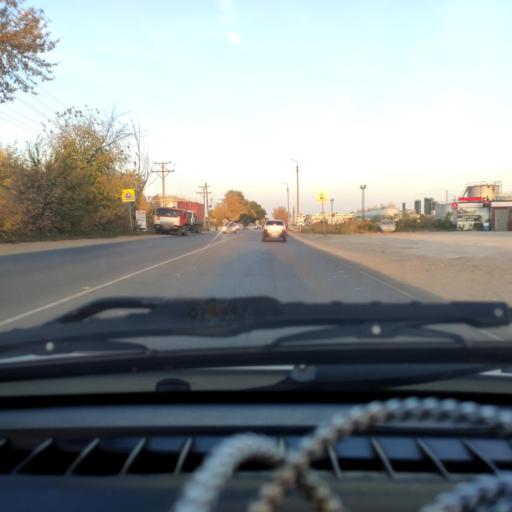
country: RU
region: Samara
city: Tol'yatti
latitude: 53.5313
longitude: 49.4608
